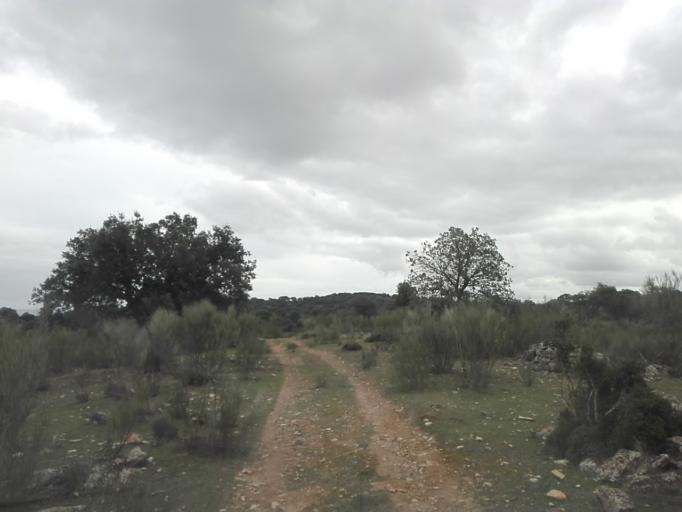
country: ES
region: Extremadura
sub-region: Provincia de Badajoz
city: Hinojosa del Valle
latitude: 38.4398
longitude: -6.1941
